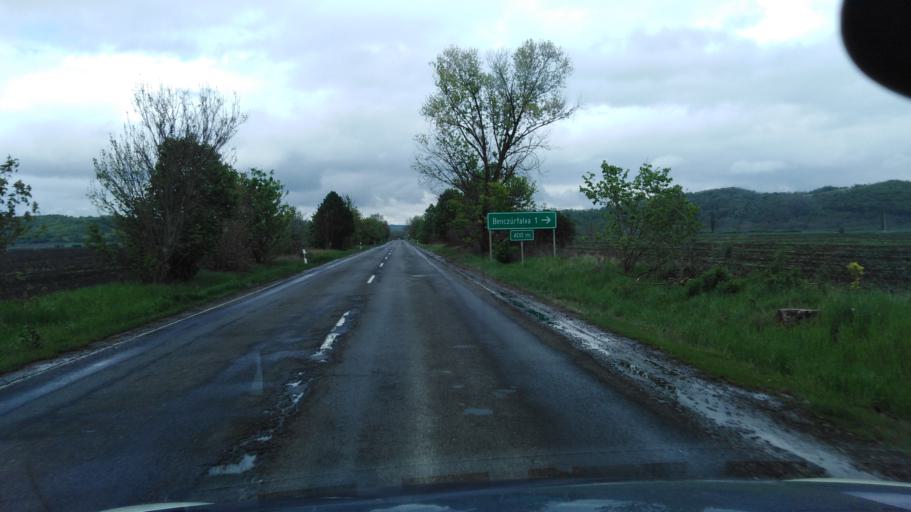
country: HU
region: Nograd
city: Szecseny
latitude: 48.1066
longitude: 19.5438
